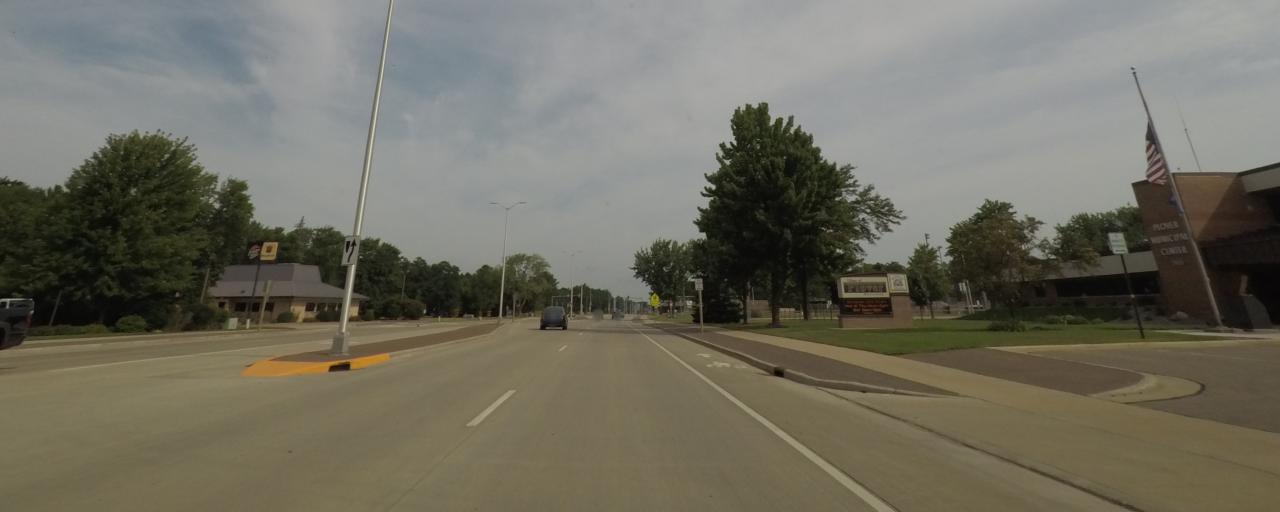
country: US
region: Wisconsin
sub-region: Portage County
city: Plover
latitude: 44.4623
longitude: -89.5438
